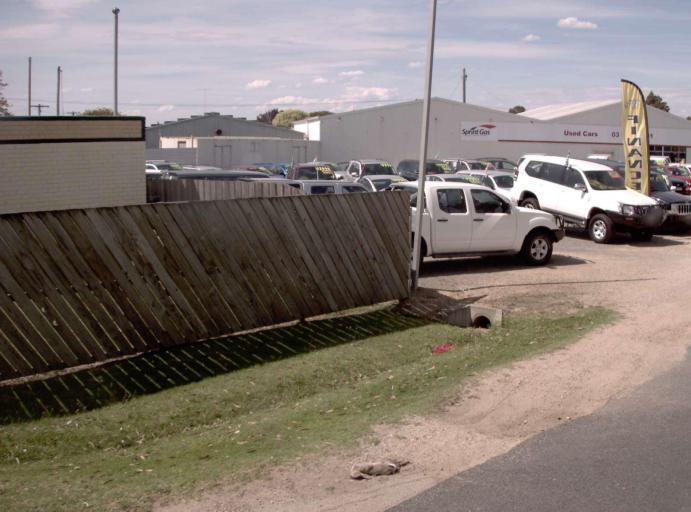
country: AU
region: Victoria
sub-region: East Gippsland
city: Bairnsdale
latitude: -37.8341
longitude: 147.6046
